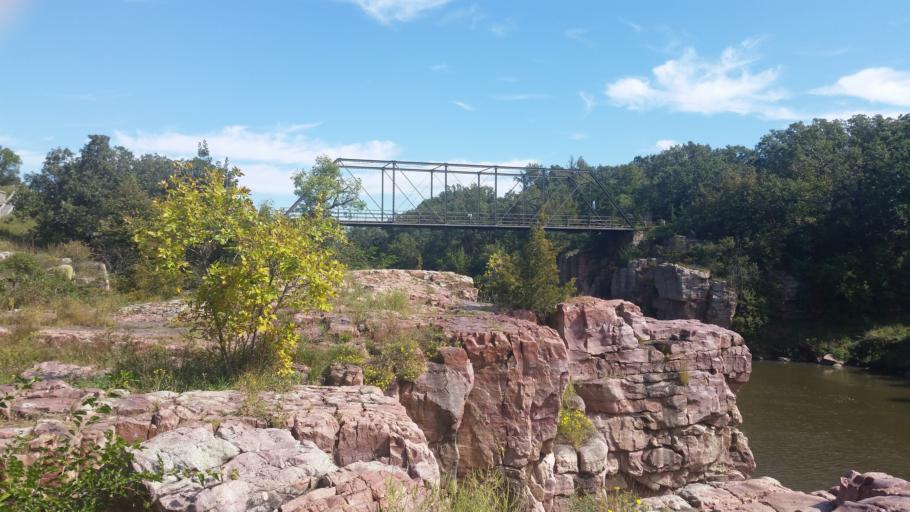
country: US
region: South Dakota
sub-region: Minnehaha County
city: Garretson
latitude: 43.7086
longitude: -96.5045
